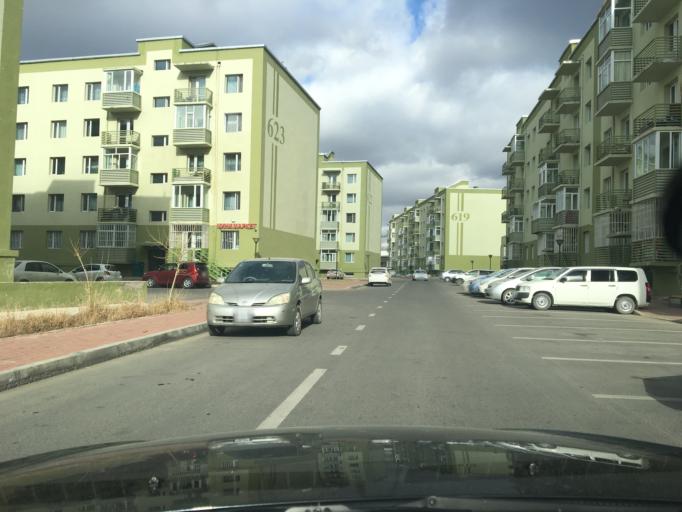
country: MN
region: Ulaanbaatar
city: Ulaanbaatar
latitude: 47.8781
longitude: 106.8464
